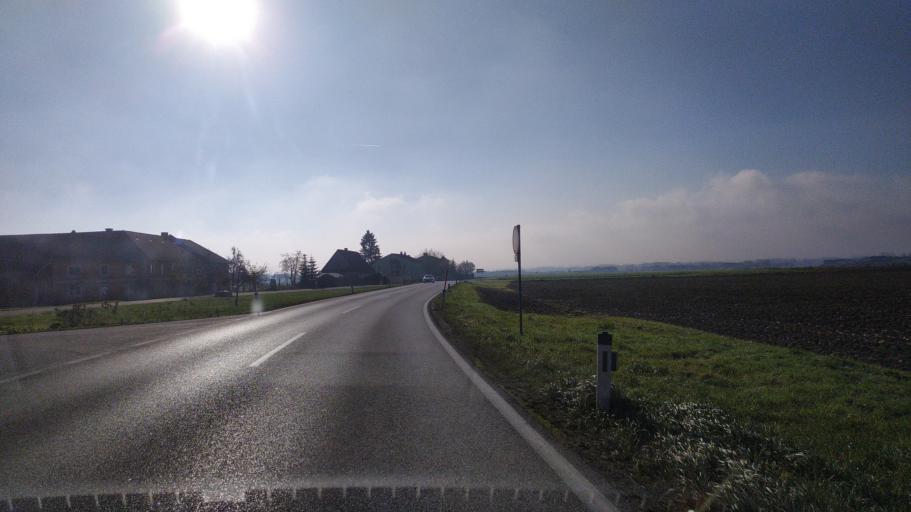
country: AT
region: Upper Austria
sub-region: Politischer Bezirk Perg
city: Perg
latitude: 48.2306
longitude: 14.6234
